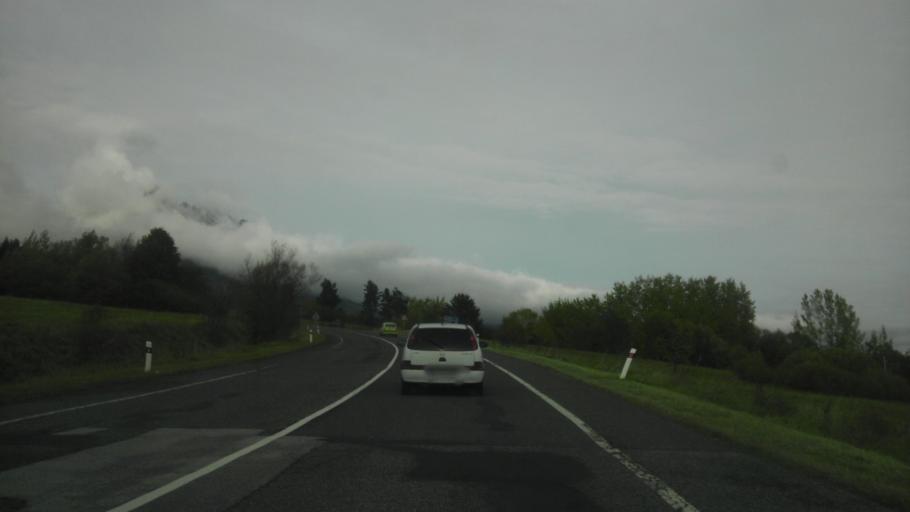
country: SK
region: Presovsky
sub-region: Okres Poprad
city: Nova Lesna
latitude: 49.1122
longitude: 20.2641
